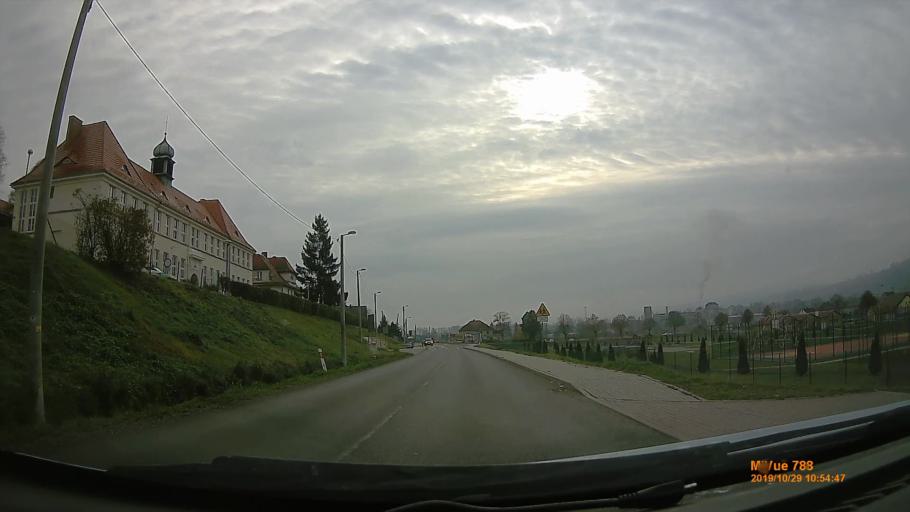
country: PL
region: Lower Silesian Voivodeship
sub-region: Powiat klodzki
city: Nowa Ruda
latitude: 50.5230
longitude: 16.4935
